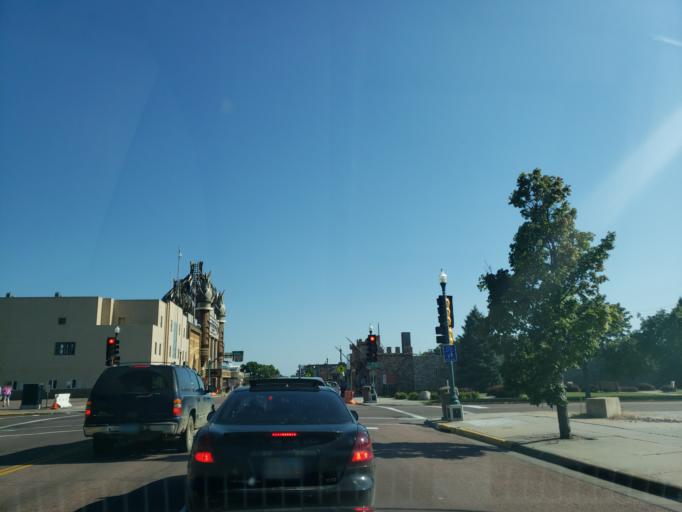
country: US
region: South Dakota
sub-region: Davison County
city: Mitchell
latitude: 43.7158
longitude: -98.0256
